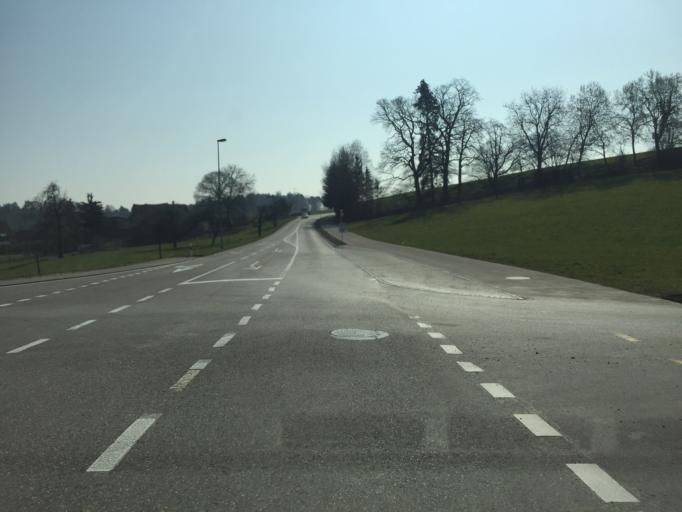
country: CH
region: Thurgau
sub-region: Frauenfeld District
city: Huttwilen
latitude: 47.5968
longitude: 8.8896
